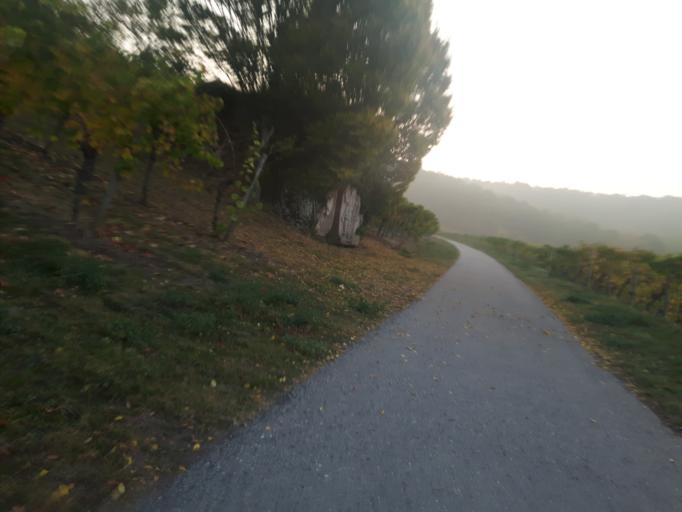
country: DE
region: Baden-Wuerttemberg
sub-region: Regierungsbezirk Stuttgart
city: Beilstein
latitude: 49.0622
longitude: 9.3238
